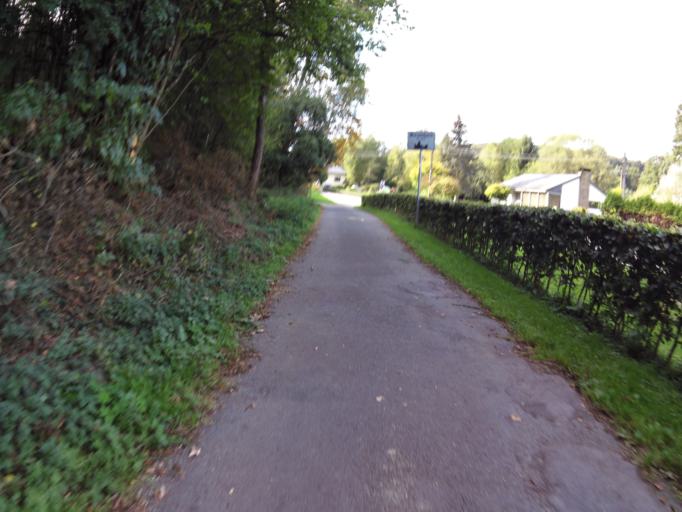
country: BE
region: Wallonia
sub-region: Province de Liege
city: Saint-Vith
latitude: 50.2633
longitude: 6.1454
